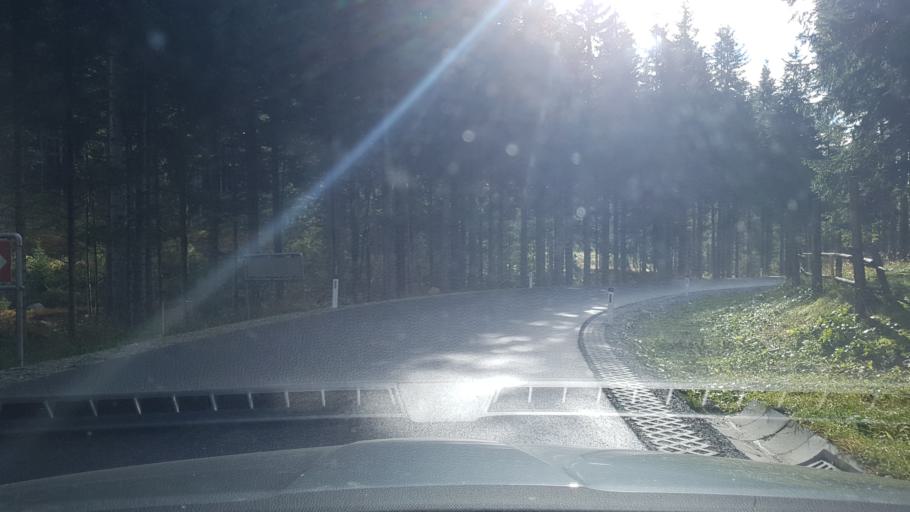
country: AT
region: Styria
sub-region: Politischer Bezirk Murau
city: Schoder
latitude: 47.2383
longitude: 14.0859
